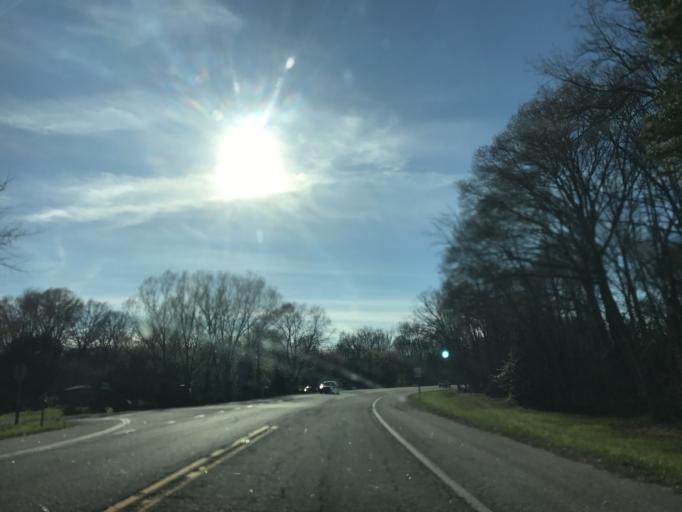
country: US
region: Maryland
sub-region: Caroline County
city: Greensboro
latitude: 39.1158
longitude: -75.7537
